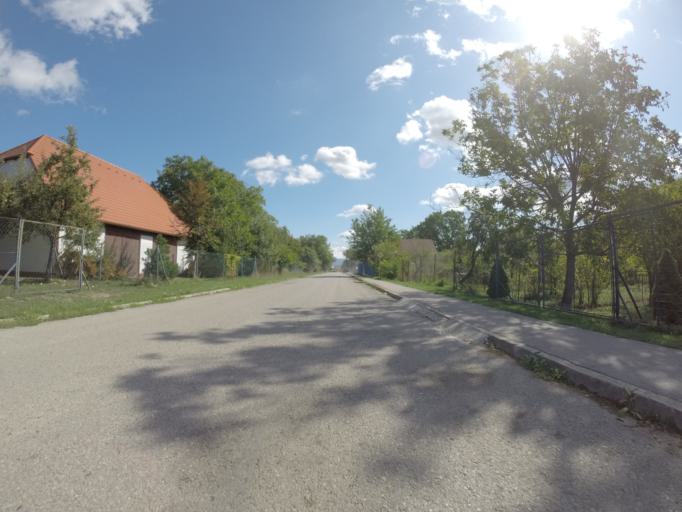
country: SK
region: Trenciansky
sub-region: Okres Nove Mesto nad Vahom
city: Nove Mesto nad Vahom
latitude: 48.7887
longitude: 17.7736
